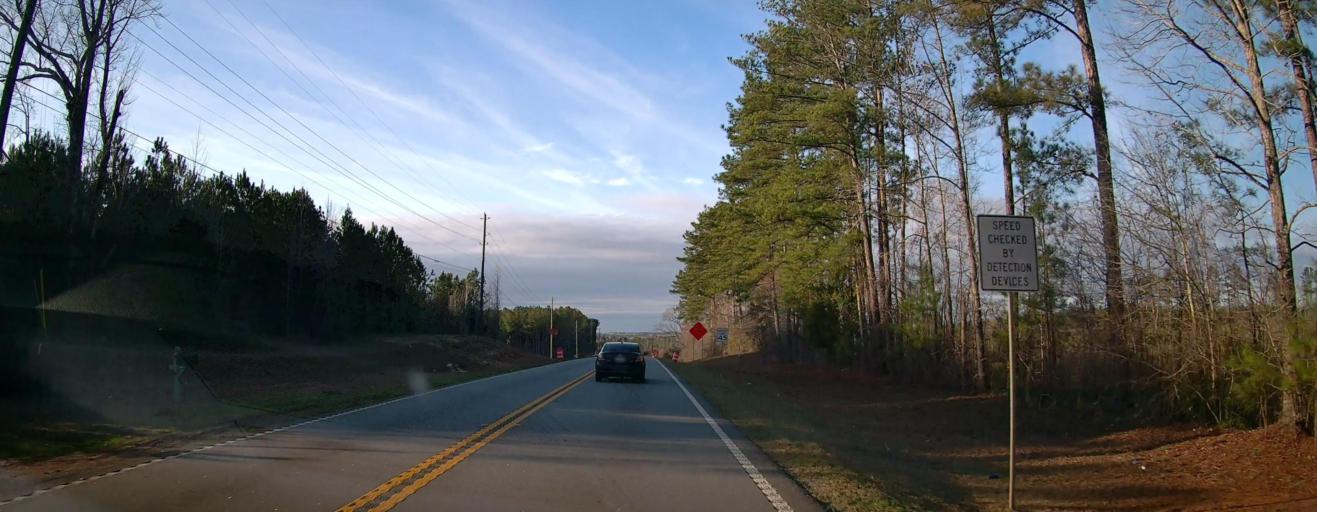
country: US
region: Georgia
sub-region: Troup County
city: West Point
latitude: 32.8710
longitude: -85.1424
